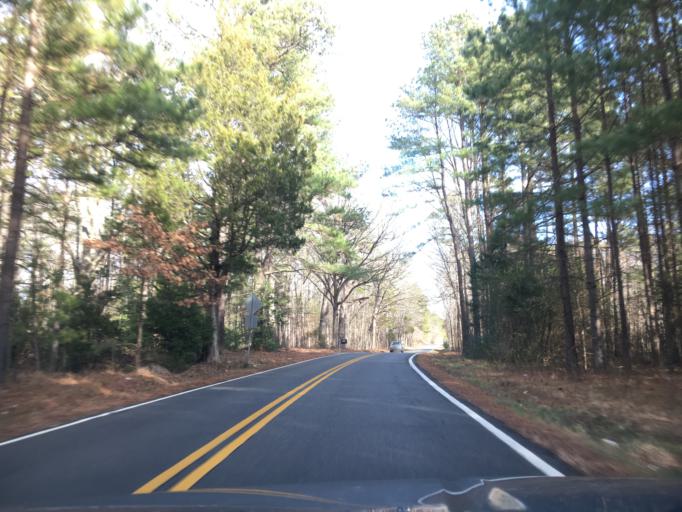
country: US
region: Virginia
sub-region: Halifax County
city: South Boston
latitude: 36.7350
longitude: -78.8606
